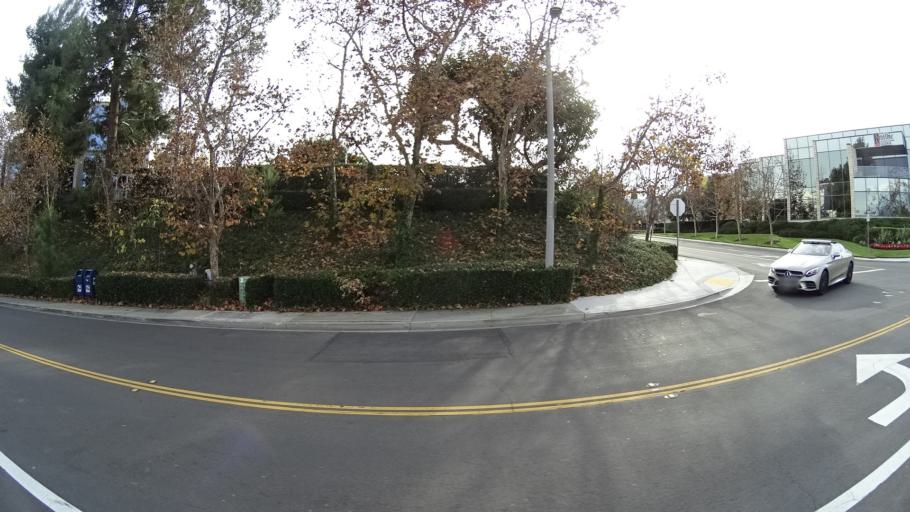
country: US
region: California
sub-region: Orange County
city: Aliso Viejo
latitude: 33.5673
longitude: -117.7246
